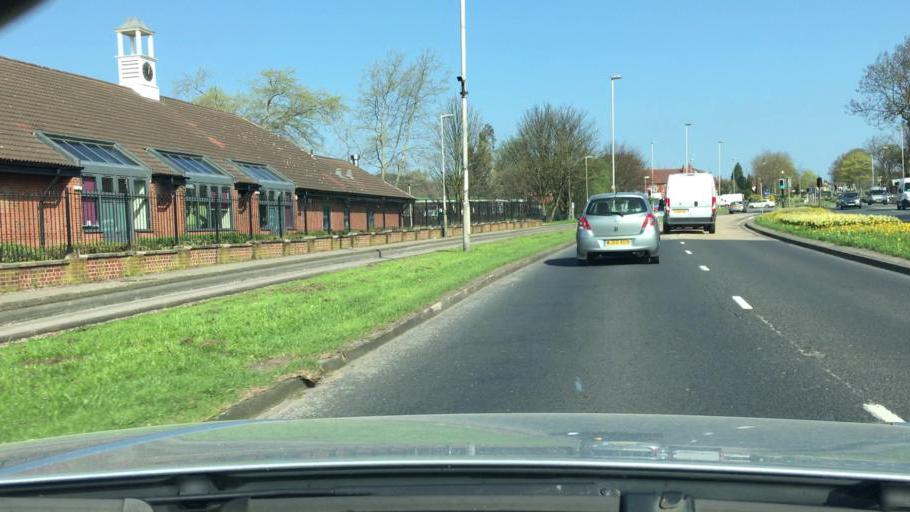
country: GB
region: England
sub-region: City and Borough of Leeds
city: Chapel Allerton
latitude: 53.8236
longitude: -1.5453
